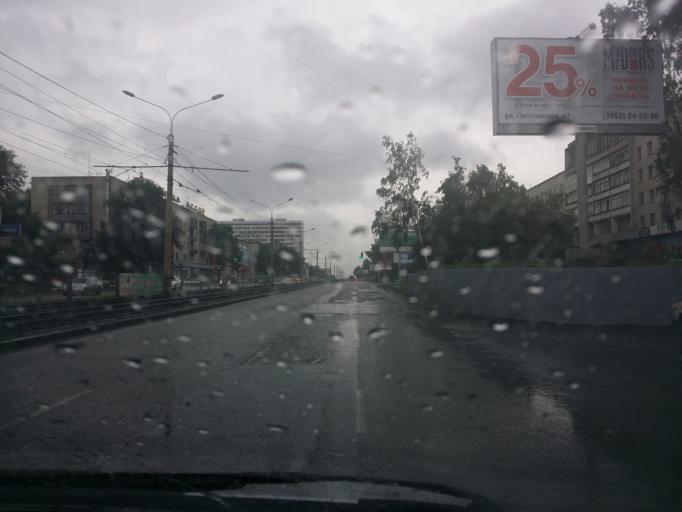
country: RU
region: Altai Krai
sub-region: Gorod Barnaulskiy
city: Barnaul
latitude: 53.3478
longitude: 83.7630
